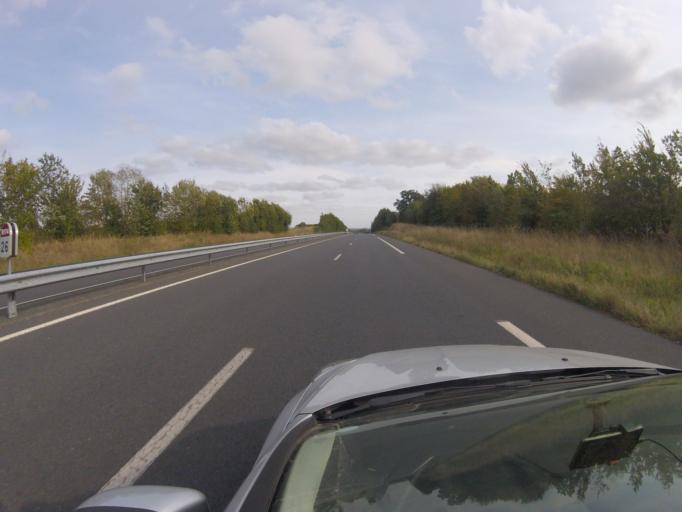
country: FR
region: Lower Normandy
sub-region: Departement de la Manche
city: Agneaux
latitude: 49.1170
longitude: -1.1607
